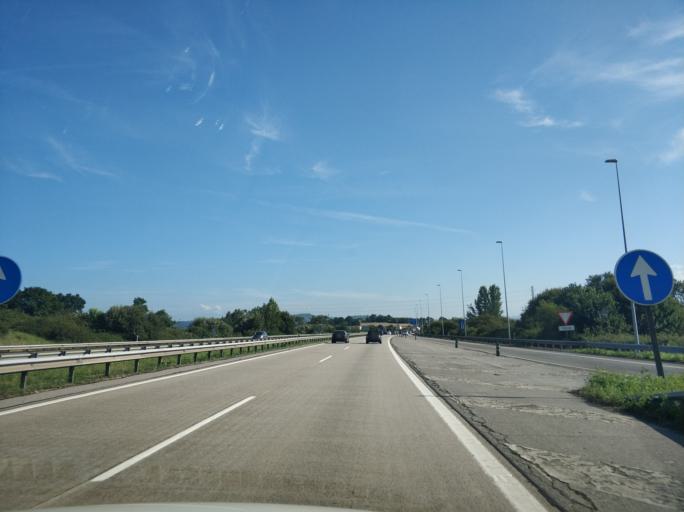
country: ES
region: Asturias
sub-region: Province of Asturias
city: Lugones
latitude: 43.4063
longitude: -5.7982
